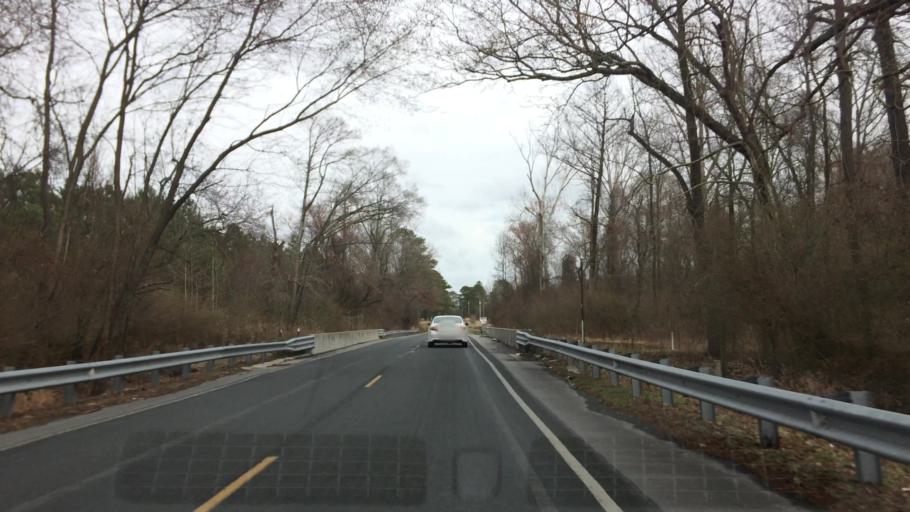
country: US
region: North Carolina
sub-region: Pitt County
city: Ayden
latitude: 35.4888
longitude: -77.3669
